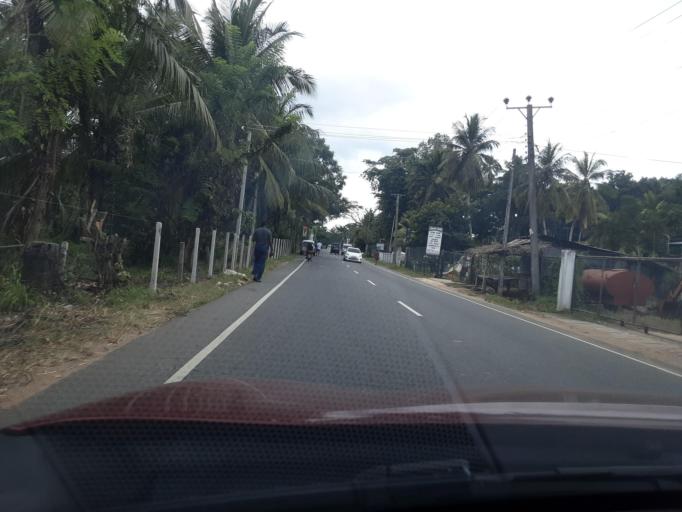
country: LK
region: North Western
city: Kurunegala
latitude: 7.4432
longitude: 80.2050
